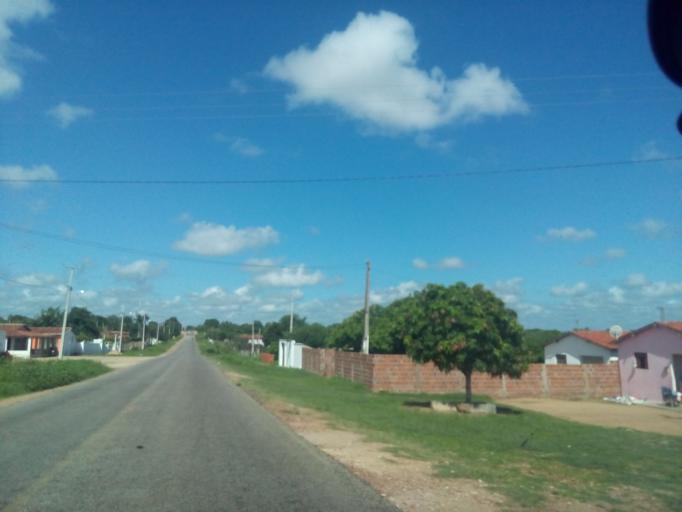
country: BR
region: Rio Grande do Norte
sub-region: Sao Paulo Do Potengi
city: Sao Paulo do Potengi
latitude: -5.9114
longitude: -35.6998
